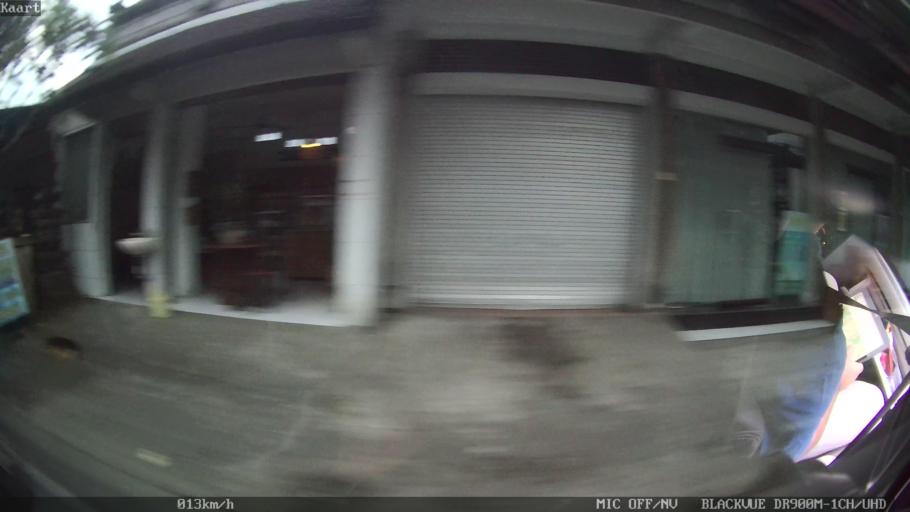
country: ID
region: Bali
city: Banjar Pande
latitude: -8.4965
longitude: 115.2456
